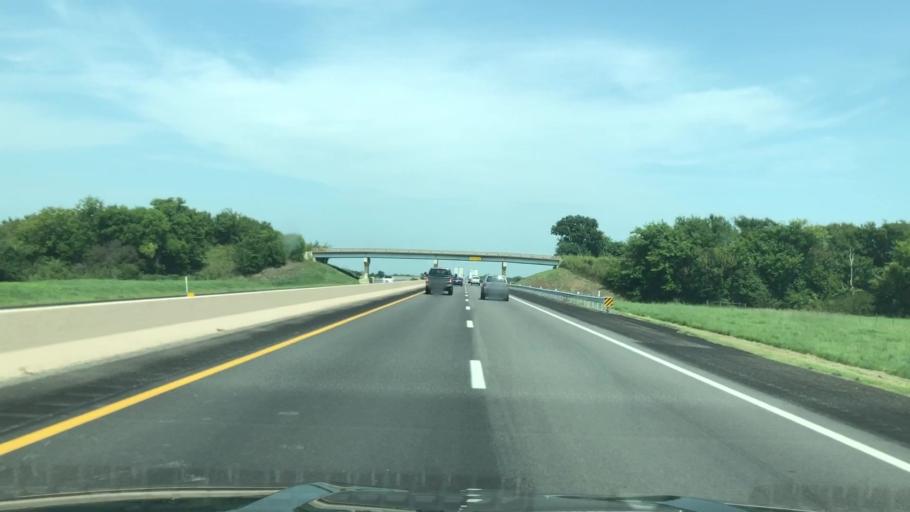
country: US
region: Oklahoma
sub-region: Ottawa County
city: Afton
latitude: 36.6758
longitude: -95.0546
